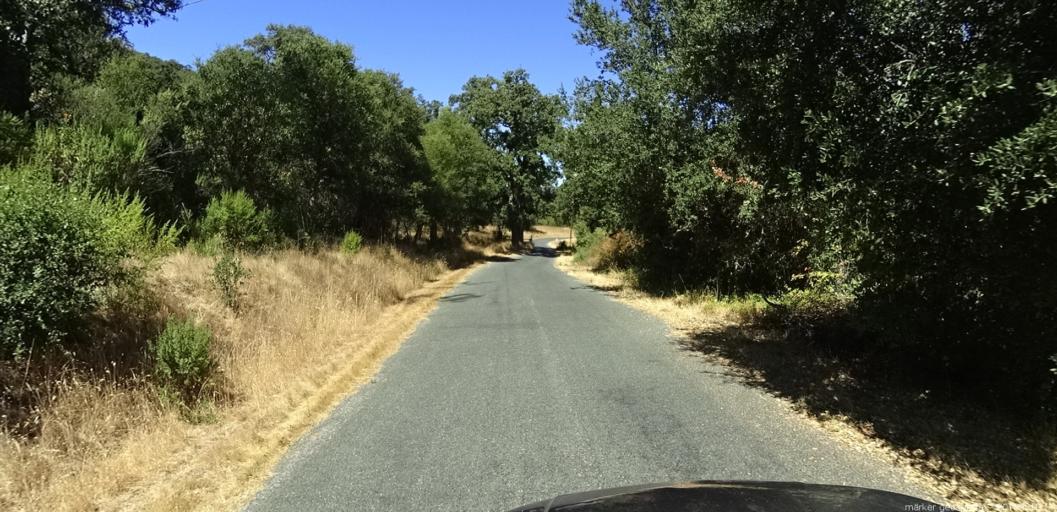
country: US
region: California
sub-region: Monterey County
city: Carmel Valley Village
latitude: 36.4340
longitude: -121.7920
